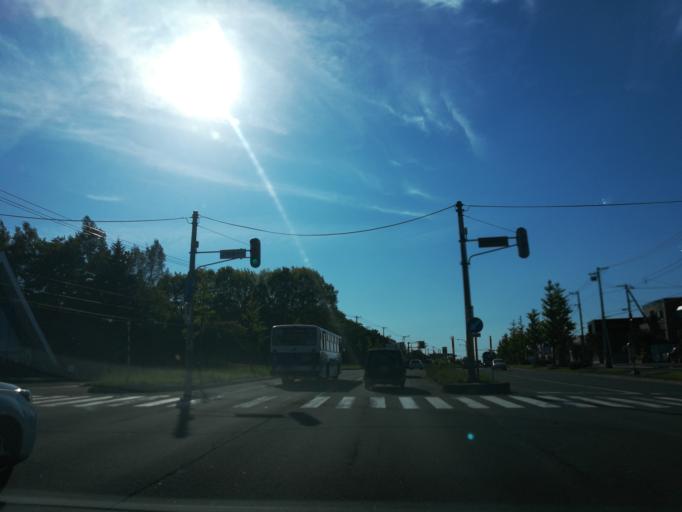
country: JP
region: Hokkaido
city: Kitahiroshima
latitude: 43.0188
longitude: 141.4794
